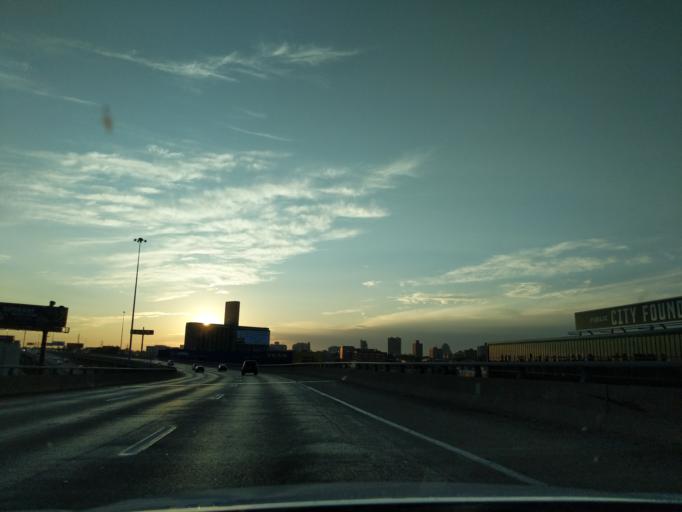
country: US
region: Missouri
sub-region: City of Saint Louis
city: St. Louis
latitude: 38.6325
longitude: -90.2386
